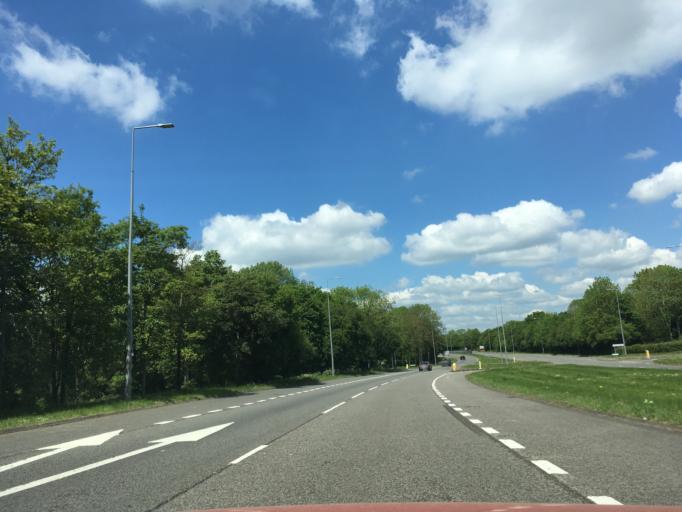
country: GB
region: England
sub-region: Milton Keynes
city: Simpson
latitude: 52.0191
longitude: -0.7256
